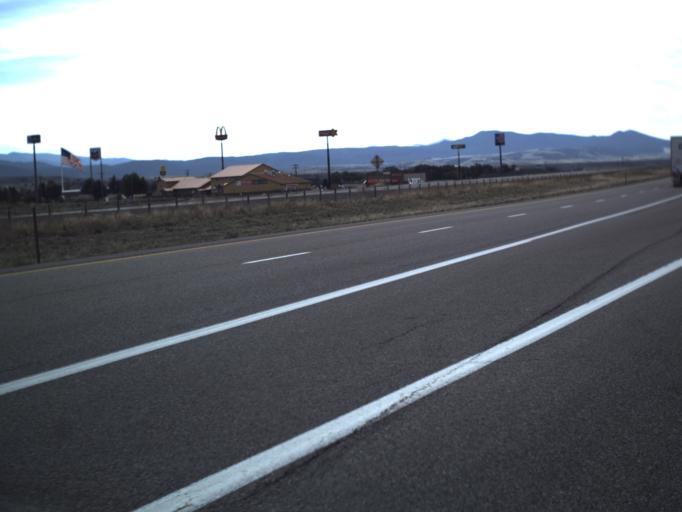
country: US
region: Utah
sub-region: Beaver County
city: Beaver
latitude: 38.2975
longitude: -112.6518
